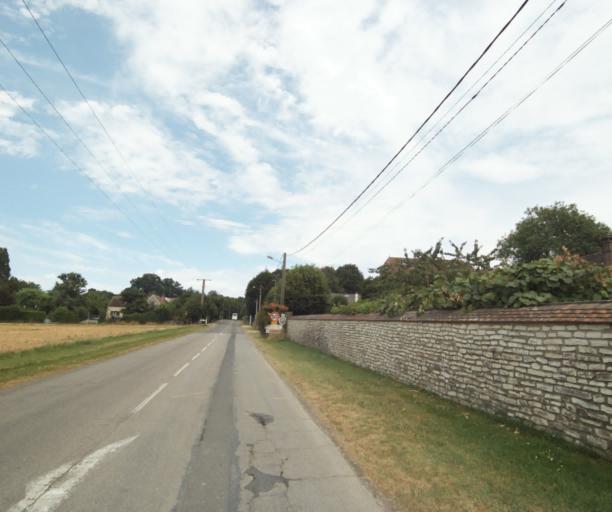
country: FR
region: Ile-de-France
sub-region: Departement de Seine-et-Marne
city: Barbizon
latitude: 48.4371
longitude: 2.5921
